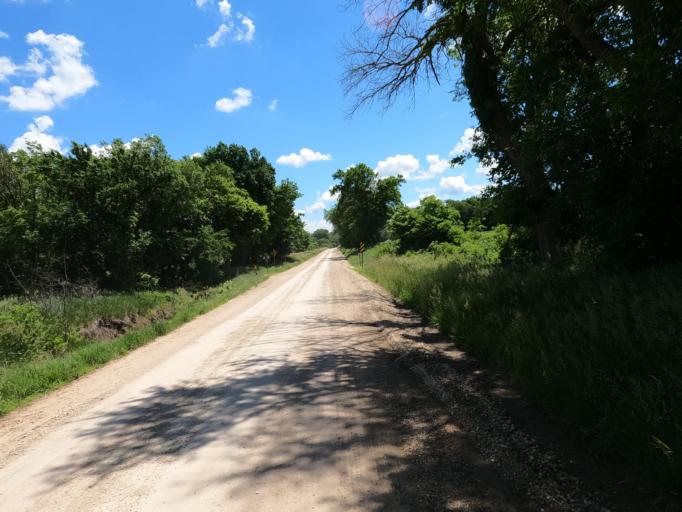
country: US
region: Kansas
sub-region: Marion County
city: Marion
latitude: 38.2454
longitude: -96.8169
